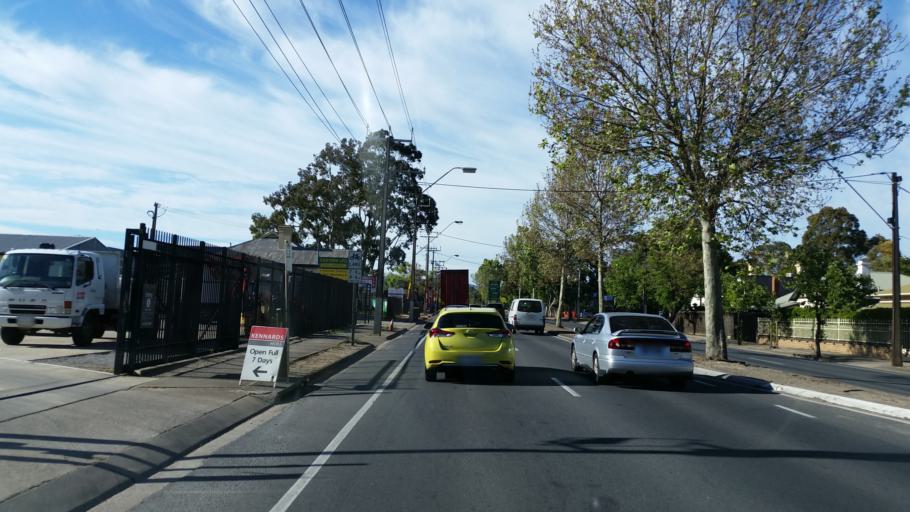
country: AU
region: South Australia
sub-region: Norwood Payneham St Peters
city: Trinity Gardens
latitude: -34.9098
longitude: 138.6402
